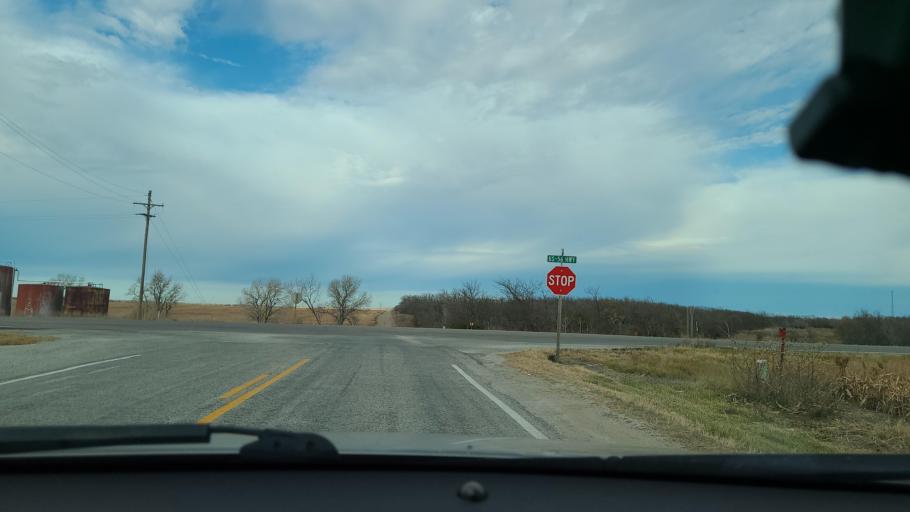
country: US
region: Kansas
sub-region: McPherson County
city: Inman
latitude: 38.3767
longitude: -97.9244
